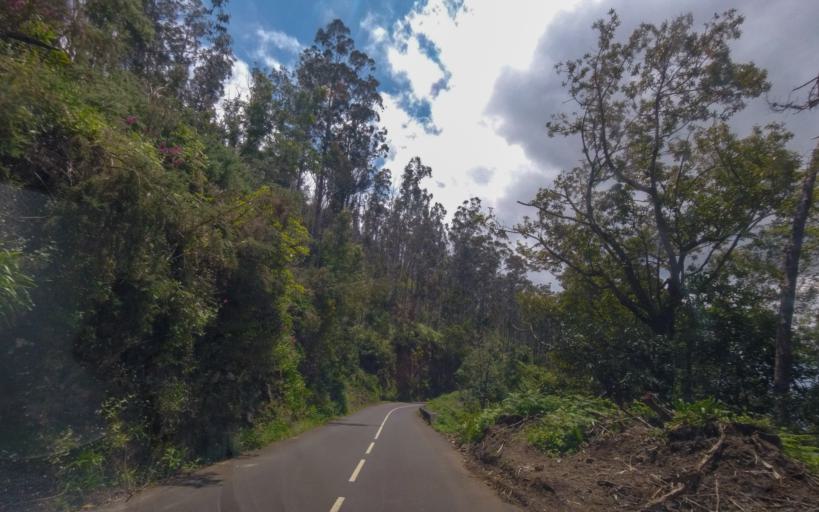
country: PT
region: Madeira
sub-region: Funchal
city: Nossa Senhora do Monte
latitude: 32.6788
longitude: -16.8805
